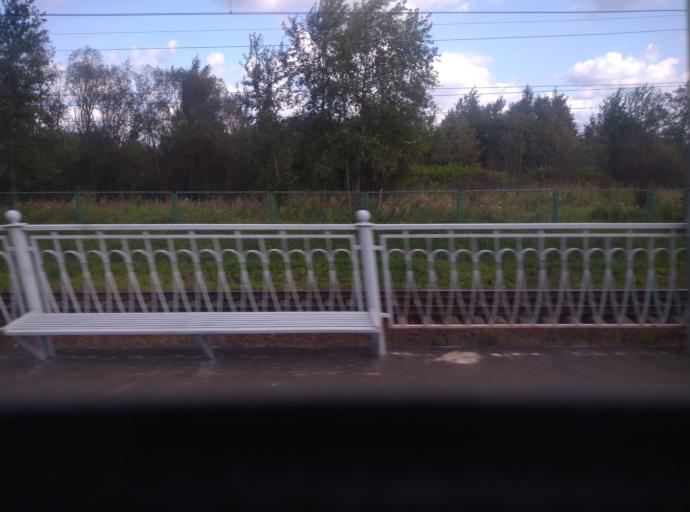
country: RU
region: St.-Petersburg
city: Kolpino
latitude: 59.7617
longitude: 30.5820
